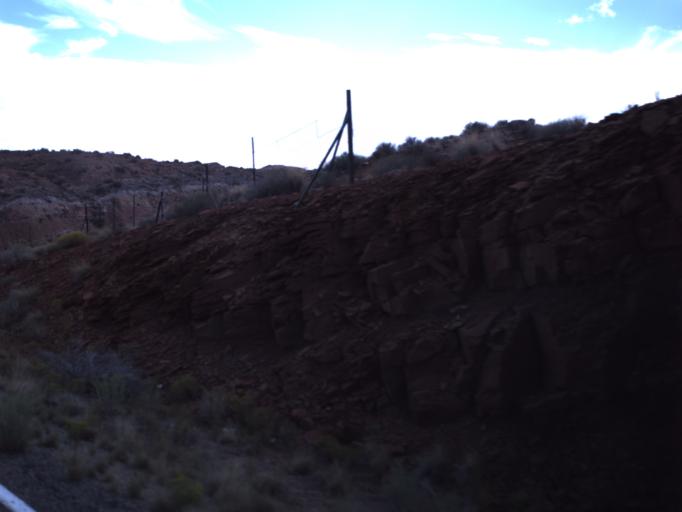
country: US
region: Utah
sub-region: San Juan County
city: Blanding
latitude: 37.2789
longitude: -109.6843
